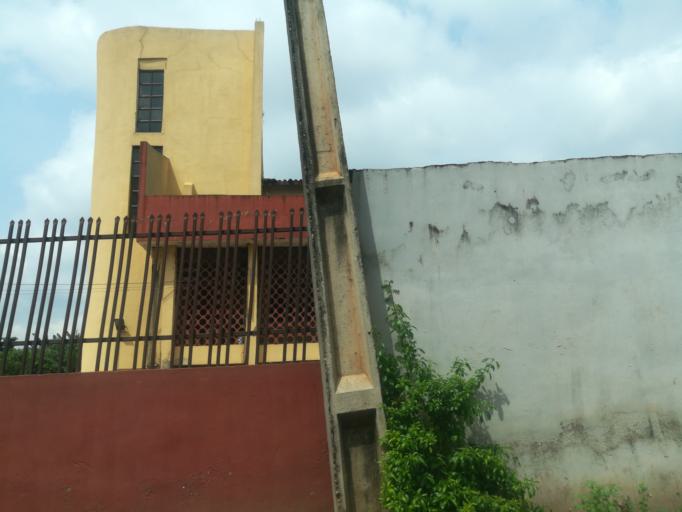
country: NG
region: Oyo
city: Ibadan
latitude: 7.4107
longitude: 3.9496
